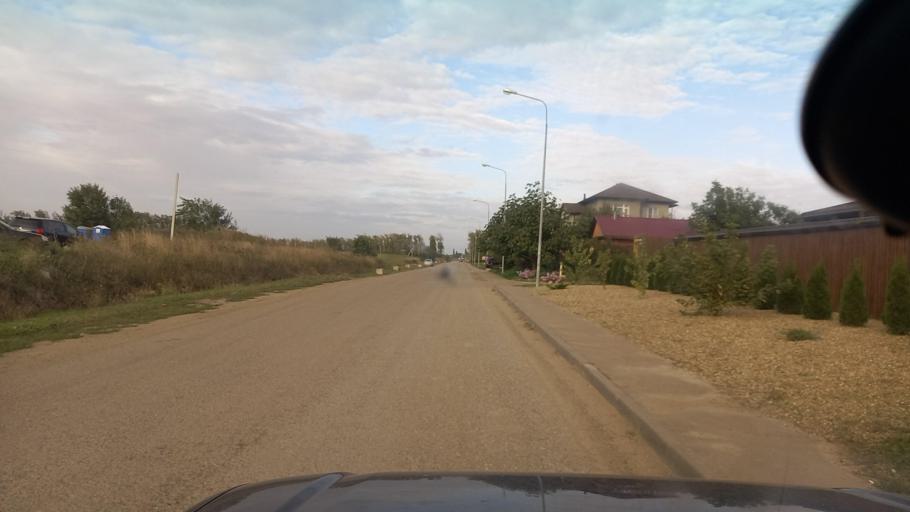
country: RU
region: Krasnodarskiy
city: Krasnodar
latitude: 45.1242
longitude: 38.9216
